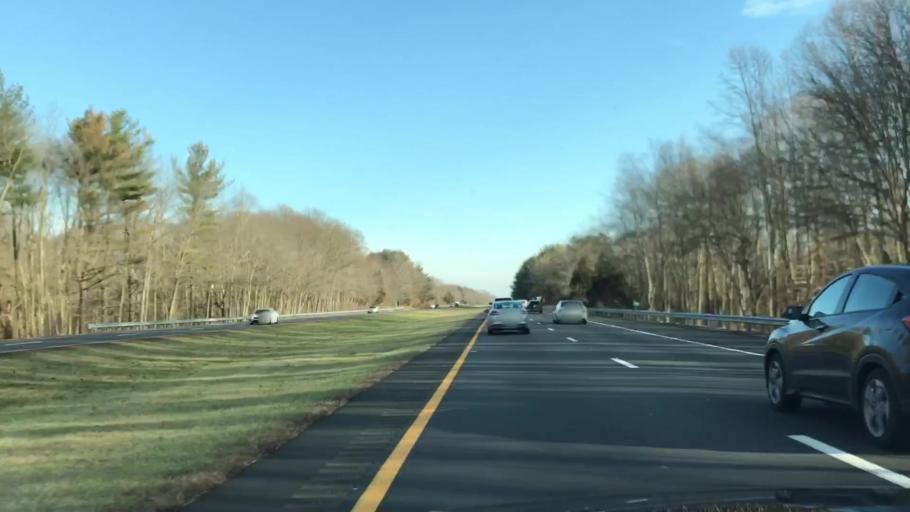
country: US
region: New Jersey
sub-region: Monmouth County
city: Shrewsbury
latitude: 40.1740
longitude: -74.4624
